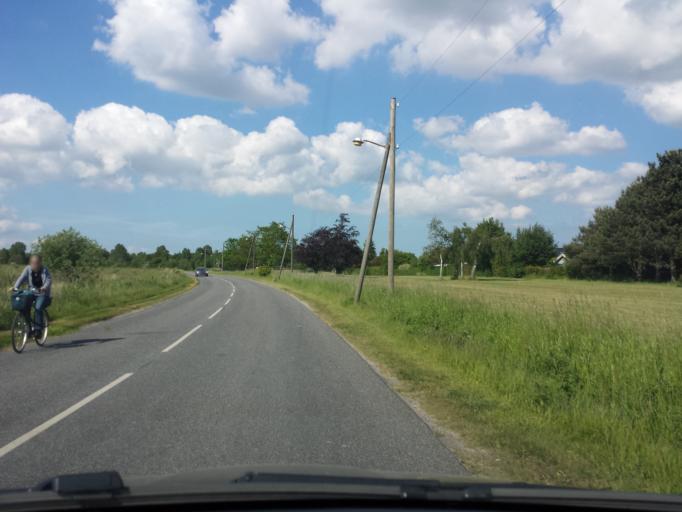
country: DK
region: Capital Region
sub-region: Ballerup Kommune
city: Ballerup
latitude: 55.7056
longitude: 12.3758
